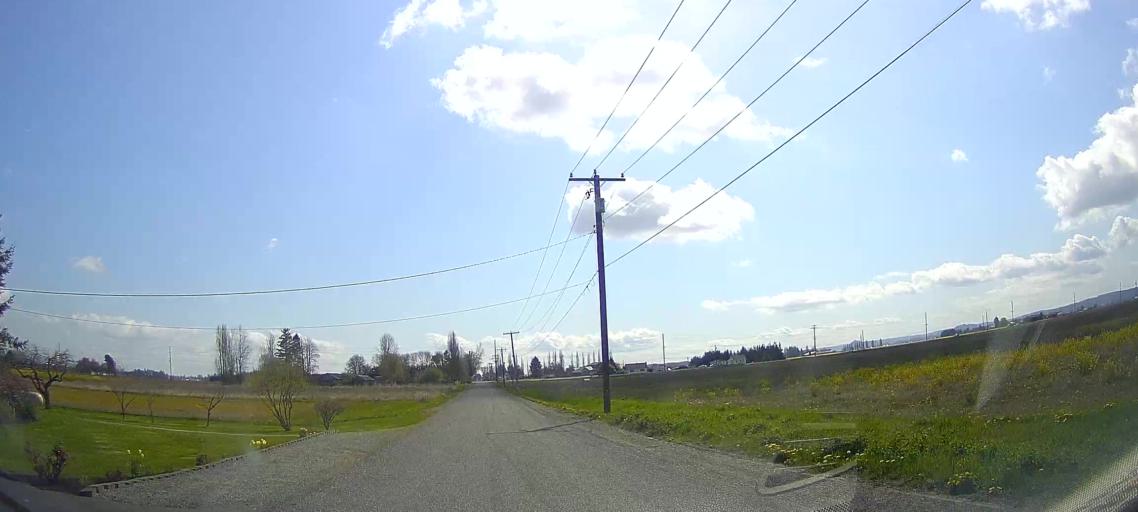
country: US
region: Washington
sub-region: Skagit County
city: Mount Vernon
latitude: 48.4458
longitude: -122.4220
